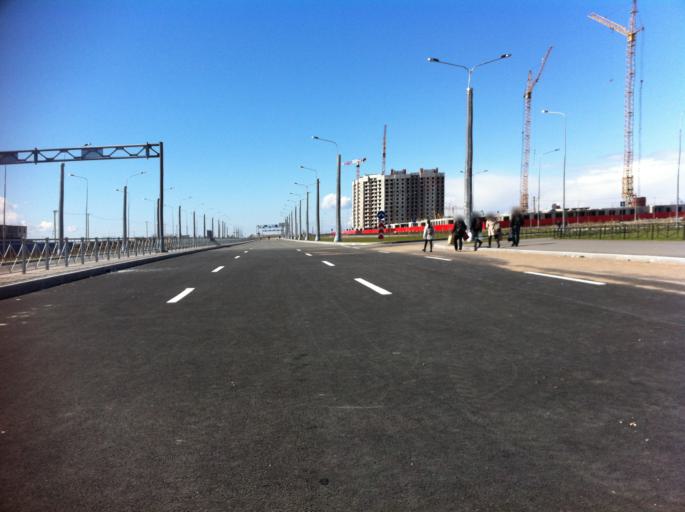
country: RU
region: St.-Petersburg
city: Uritsk
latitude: 59.8650
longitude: 30.1638
